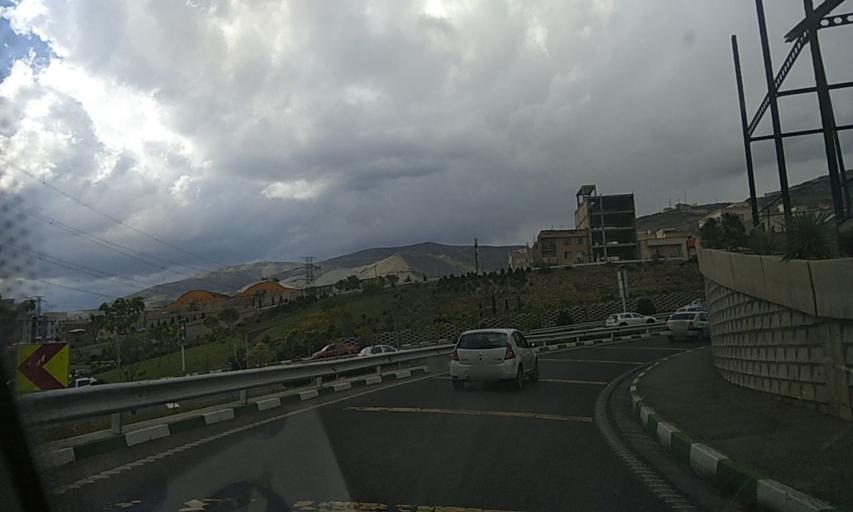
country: IR
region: Tehran
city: Tajrish
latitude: 35.7709
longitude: 51.3191
